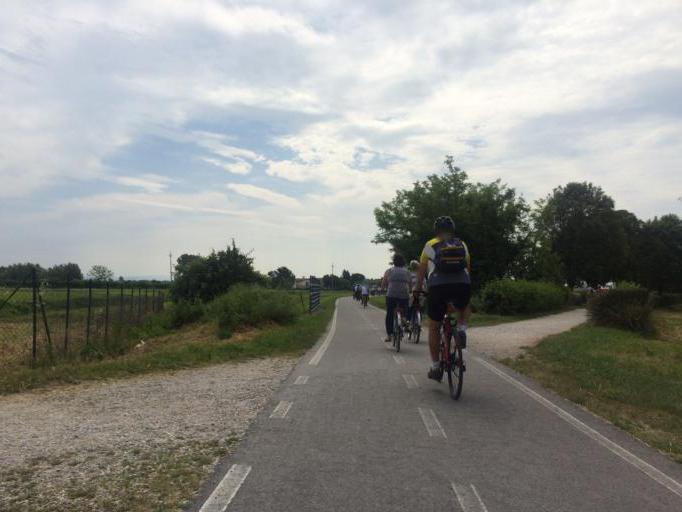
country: IT
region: Friuli Venezia Giulia
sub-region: Provincia di Udine
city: Aquileia
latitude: 45.7709
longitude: 13.3710
